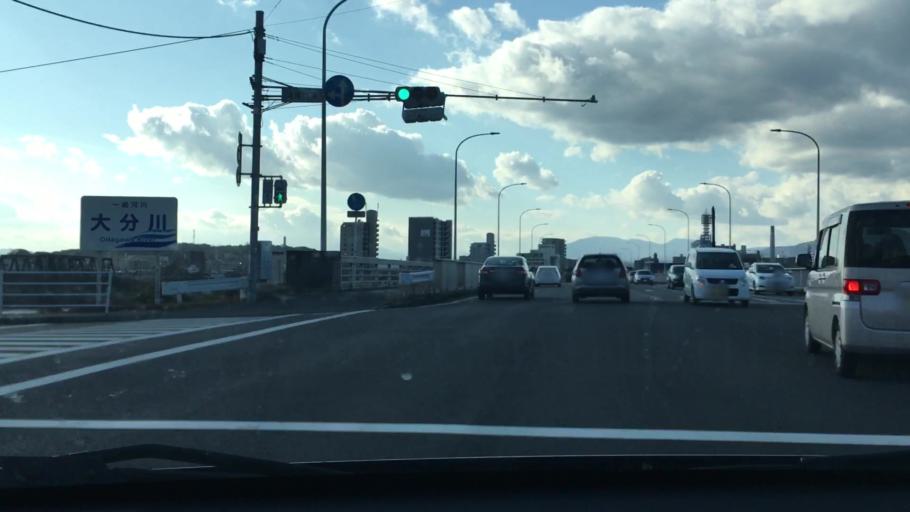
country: JP
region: Oita
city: Oita
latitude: 33.2320
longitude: 131.6259
